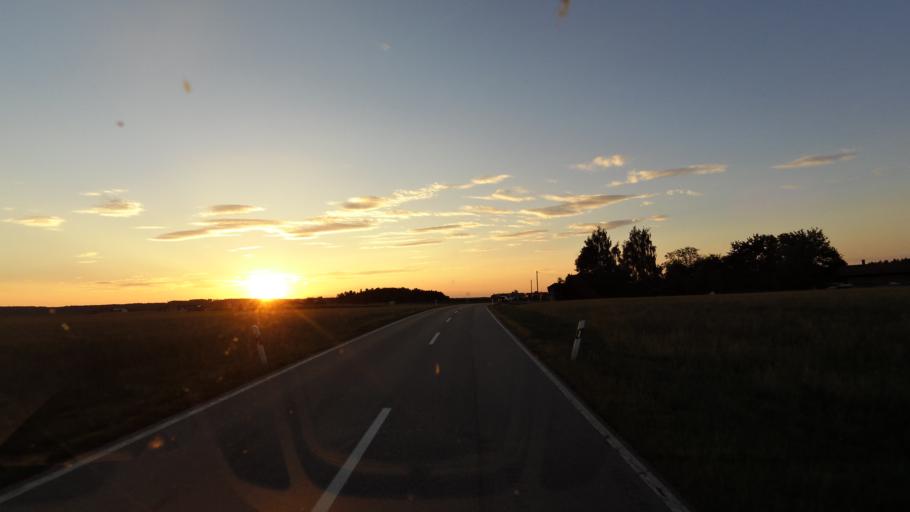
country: DE
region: Bavaria
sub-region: Upper Bavaria
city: Taufkirchen
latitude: 48.1207
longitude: 12.4649
